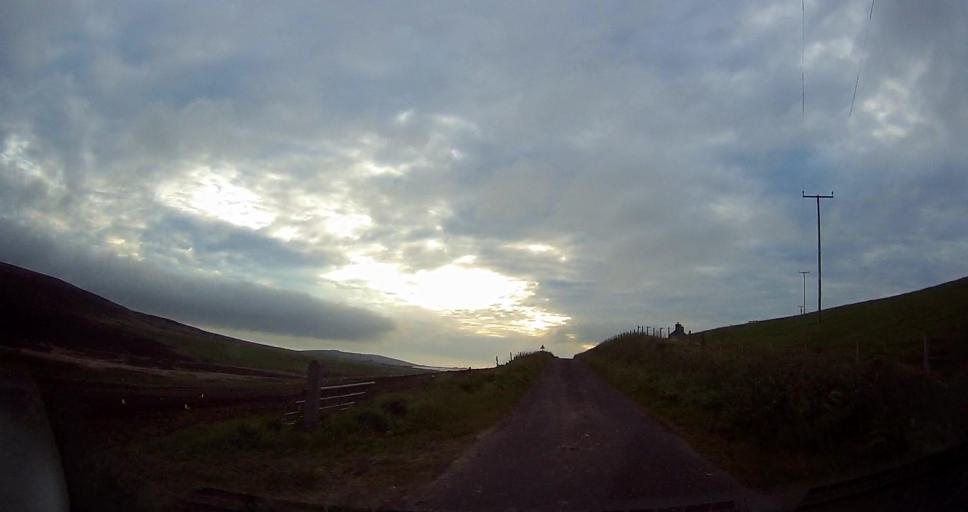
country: GB
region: Scotland
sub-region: Orkney Islands
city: Stromness
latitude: 59.1008
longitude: -3.2068
